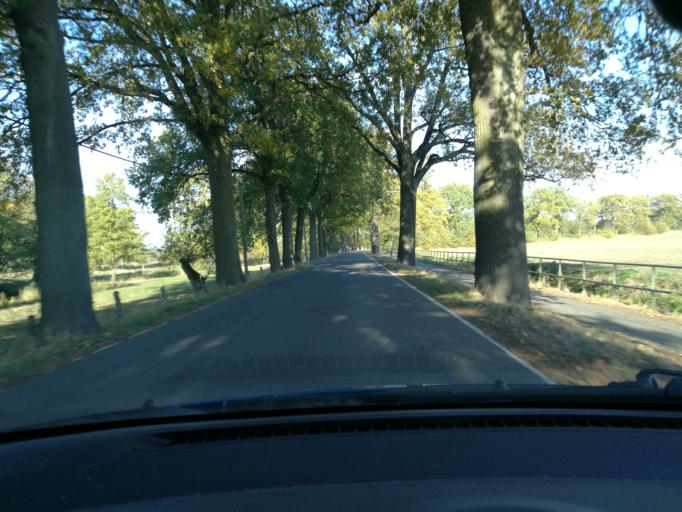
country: DE
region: Brandenburg
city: Lenzen
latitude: 53.1090
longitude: 11.4275
